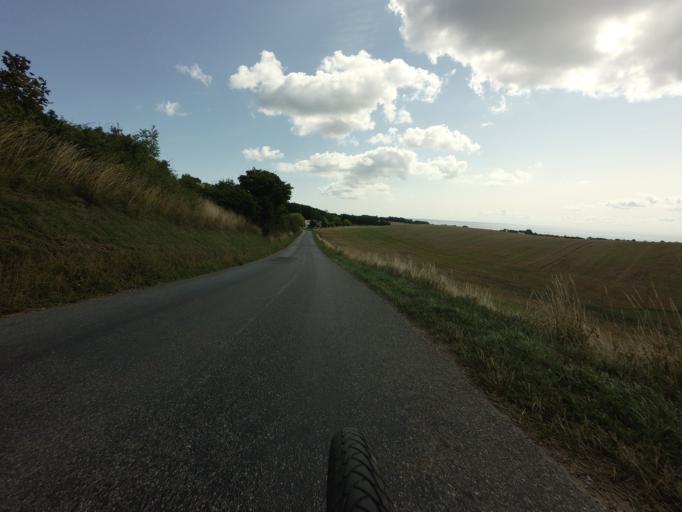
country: DK
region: Zealand
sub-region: Vordingborg Kommune
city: Stege
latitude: 54.9597
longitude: 12.5276
